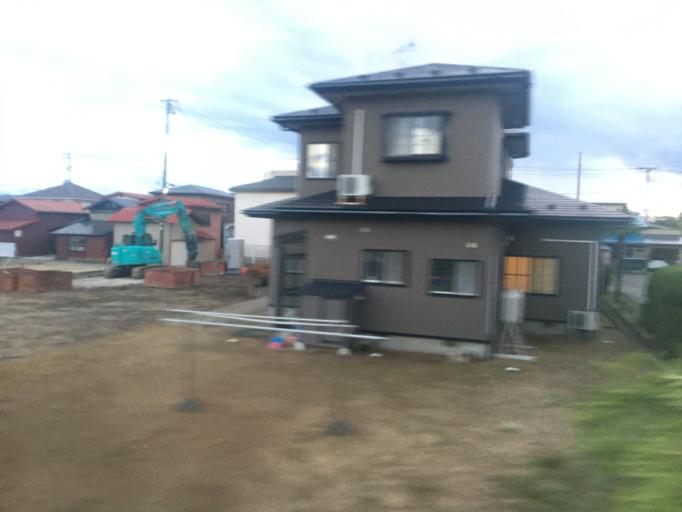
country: JP
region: Akita
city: Tenno
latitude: 39.9053
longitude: 139.9527
